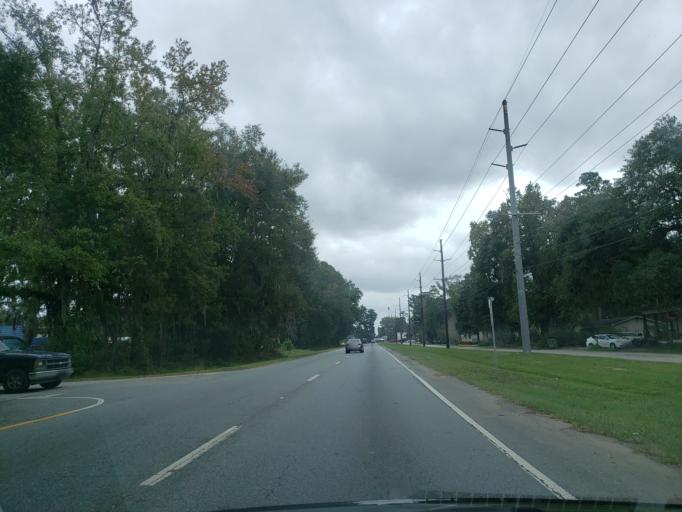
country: US
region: Georgia
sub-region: Chatham County
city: Pooler
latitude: 32.1147
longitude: -81.2471
